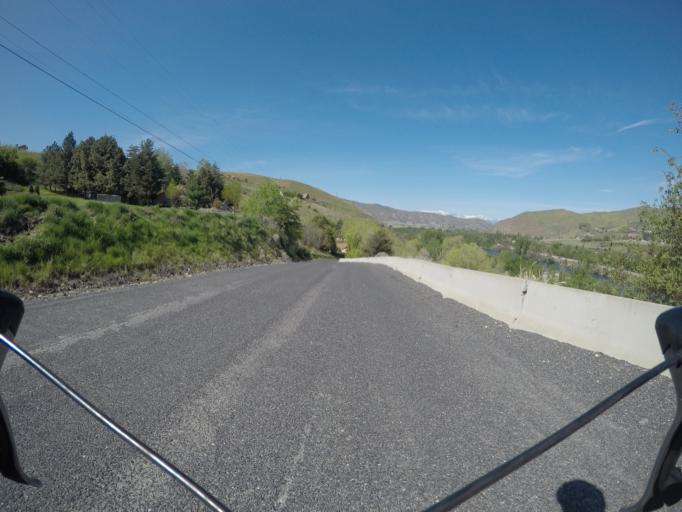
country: US
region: Washington
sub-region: Chelan County
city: West Wenatchee
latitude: 47.4771
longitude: -120.3859
